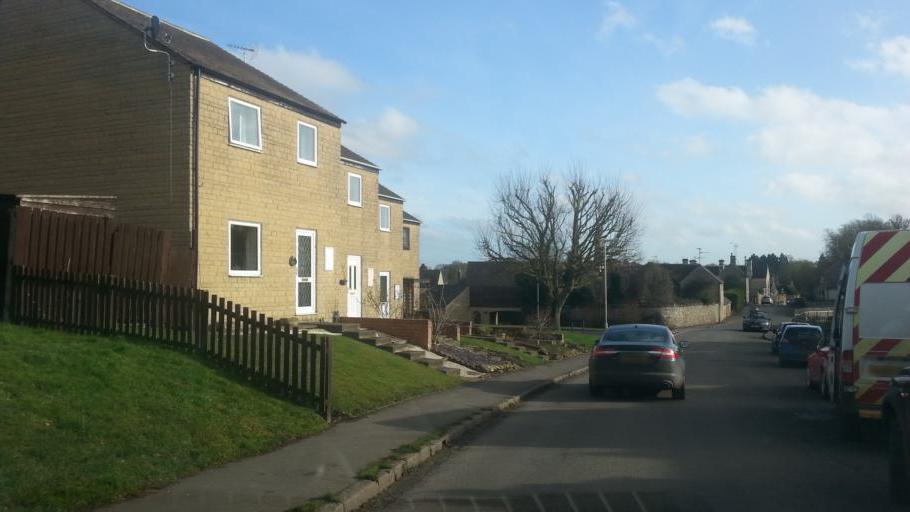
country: GB
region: England
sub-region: District of Rutland
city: Ketton
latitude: 52.6283
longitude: -0.5563
